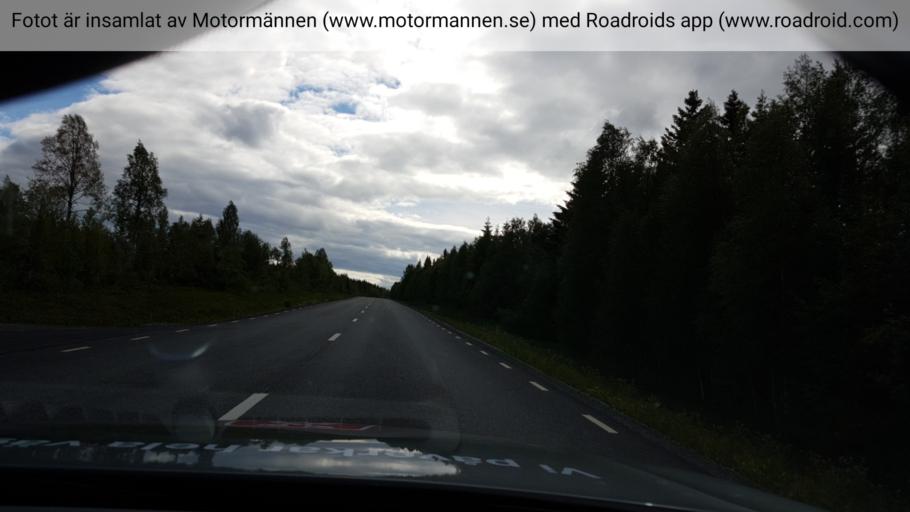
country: SE
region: Jaemtland
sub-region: Stroemsunds Kommun
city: Stroemsund
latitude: 64.1182
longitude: 15.6218
